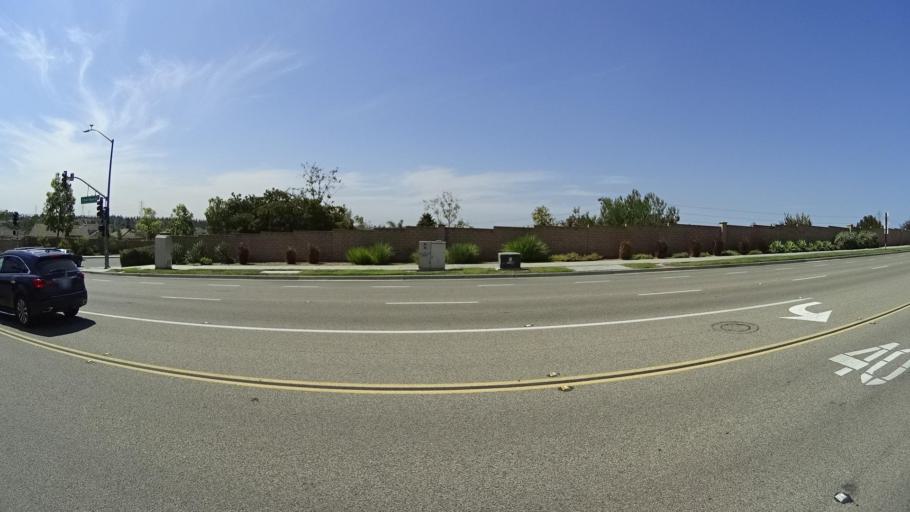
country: US
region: California
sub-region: San Diego County
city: La Presa
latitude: 32.6672
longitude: -116.9721
